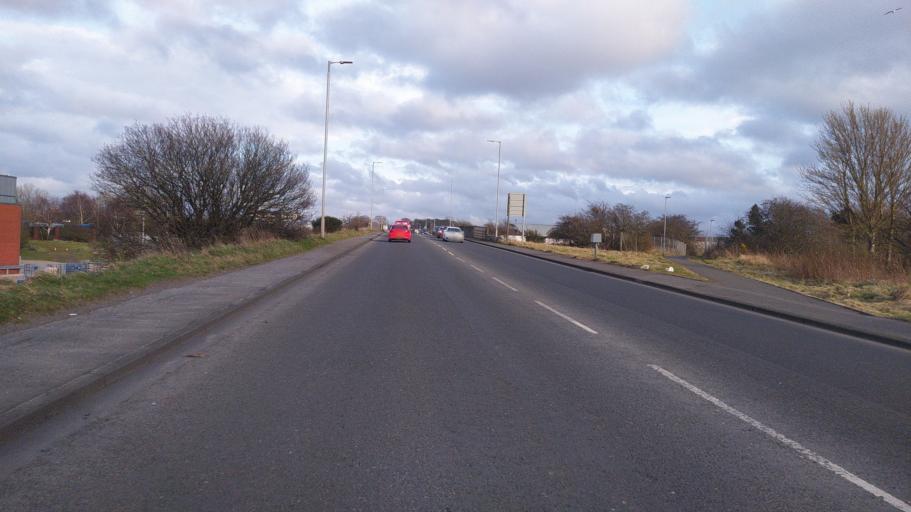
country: GB
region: Scotland
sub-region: South Ayrshire
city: Prestwick
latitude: 55.4777
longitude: -4.5957
